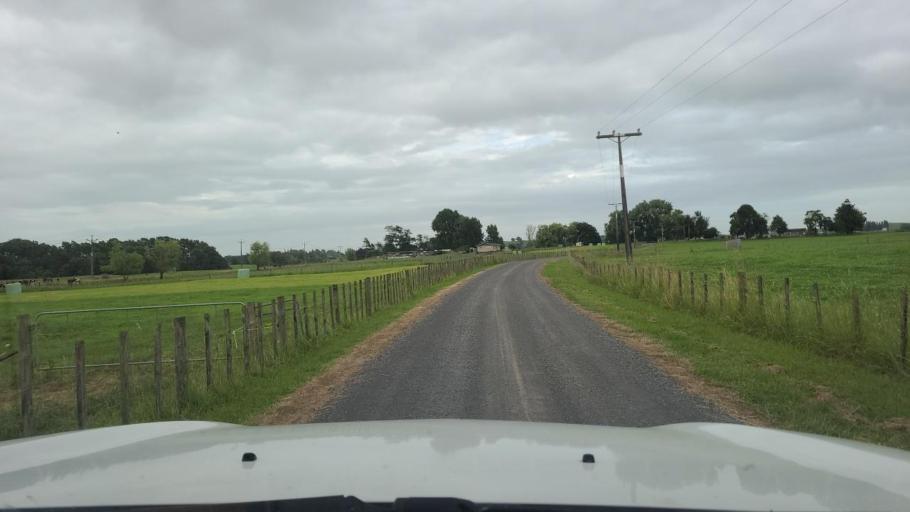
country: NZ
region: Waikato
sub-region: Hauraki District
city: Paeroa
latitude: -37.5719
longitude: 175.6674
